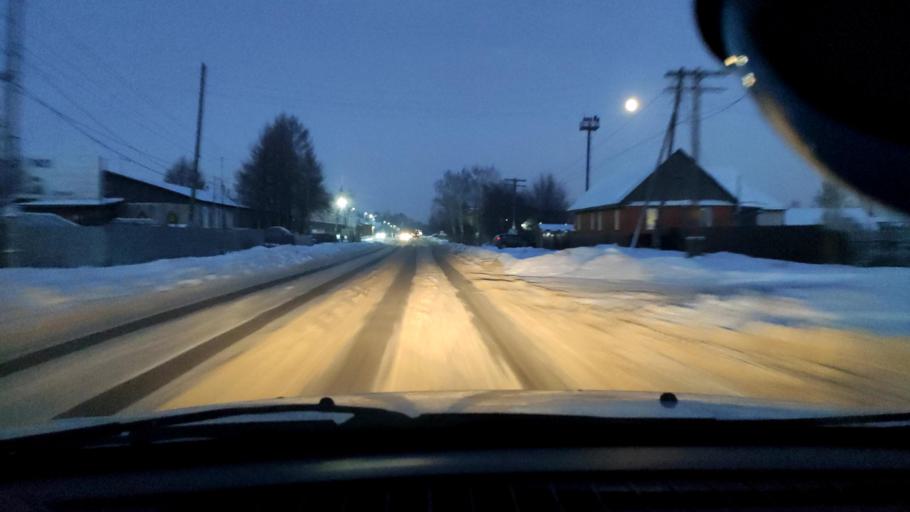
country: RU
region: Perm
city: Kultayevo
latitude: 57.8894
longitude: 55.9271
